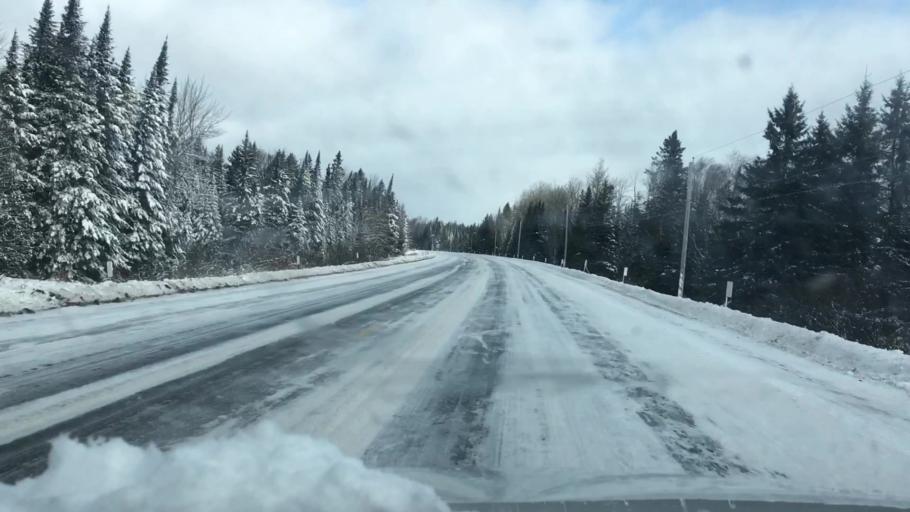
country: US
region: Maine
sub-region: Aroostook County
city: Van Buren
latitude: 47.0681
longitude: -67.9871
